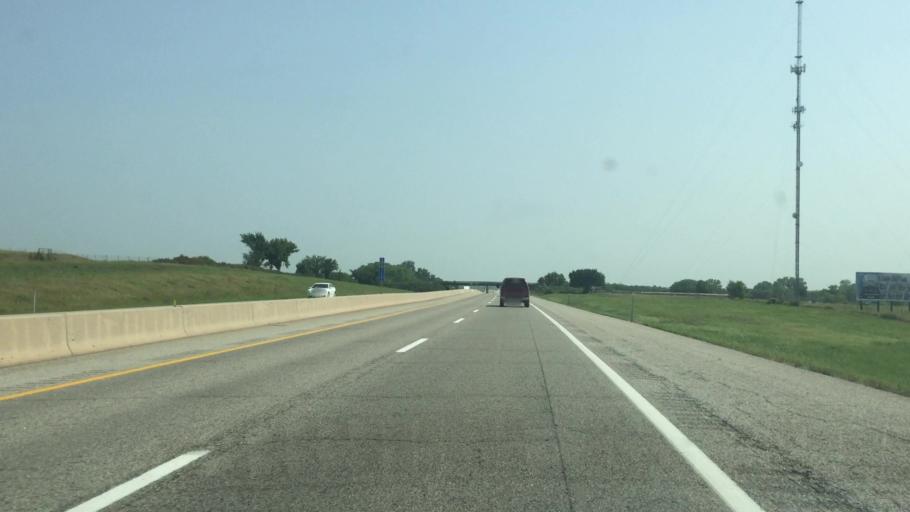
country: US
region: Kansas
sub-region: Lyon County
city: Emporia
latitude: 38.3326
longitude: -96.3040
